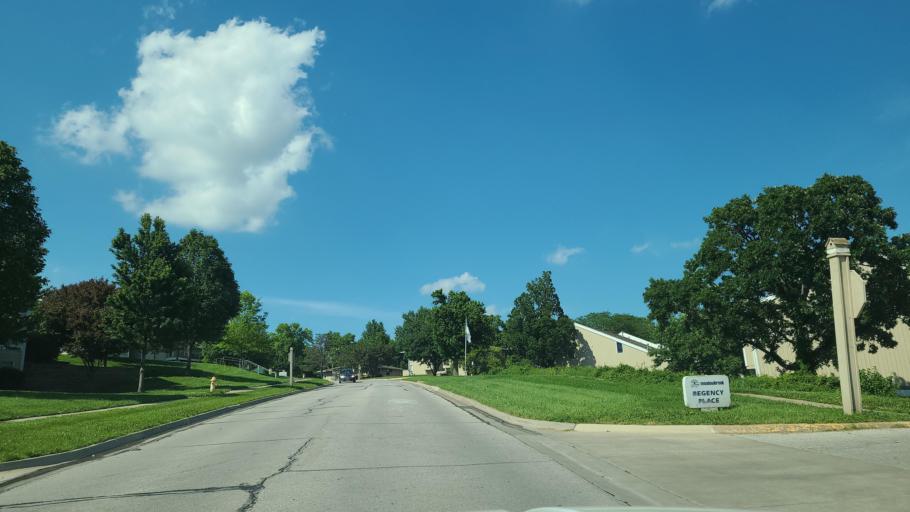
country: US
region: Kansas
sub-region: Douglas County
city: Lawrence
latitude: 38.9585
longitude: -95.2669
